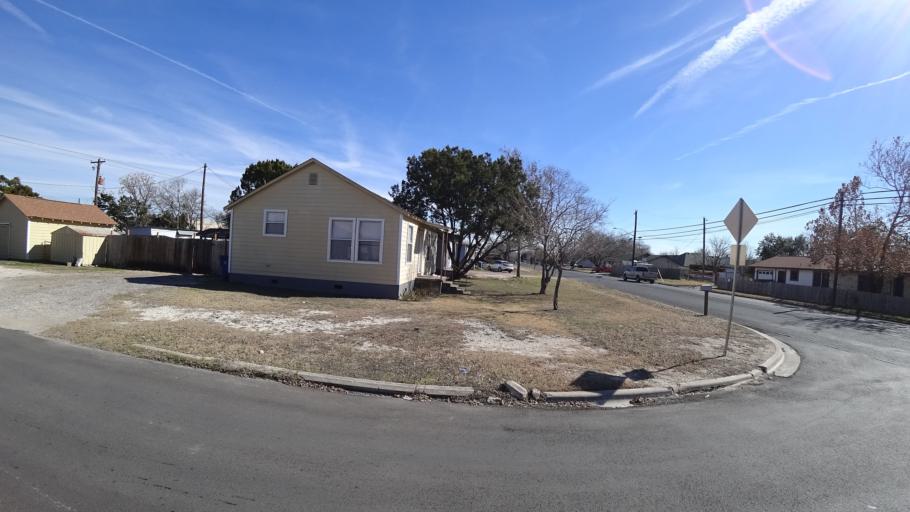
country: US
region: Texas
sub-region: Travis County
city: Wells Branch
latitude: 30.3742
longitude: -97.6859
